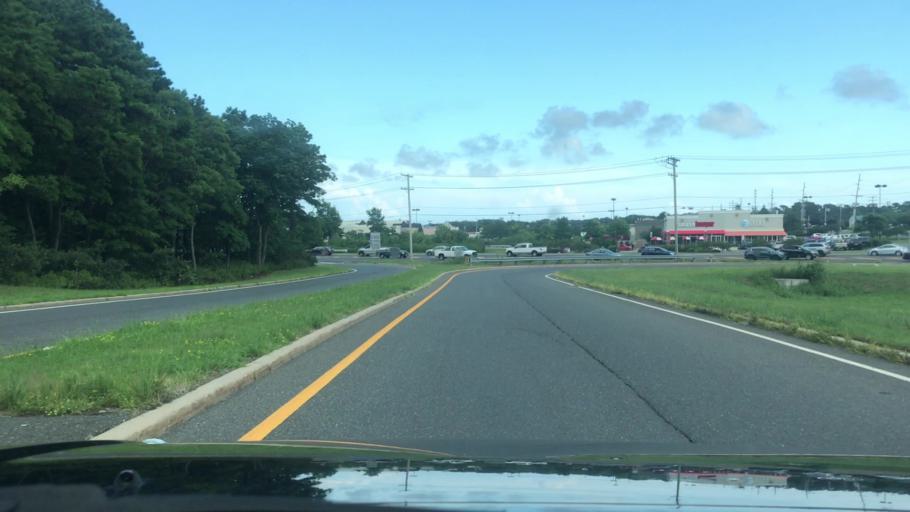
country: US
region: New Jersey
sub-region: Ocean County
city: Leisure Village East
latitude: 40.0592
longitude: -74.1455
